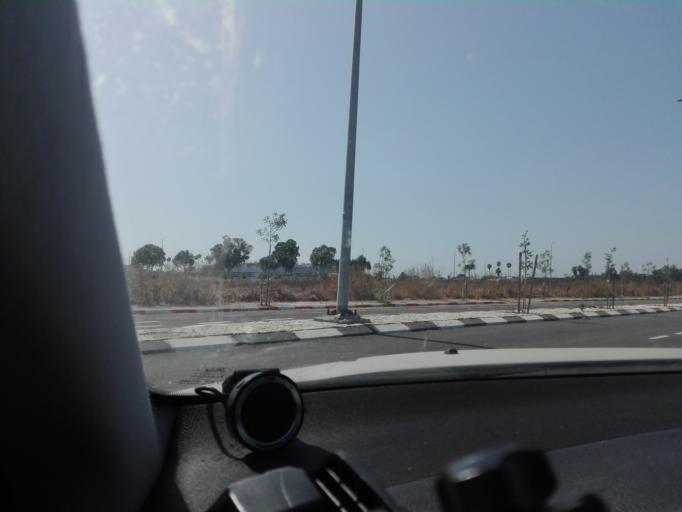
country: IL
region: Central District
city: Bene 'Ayish
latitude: 31.7279
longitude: 34.7585
